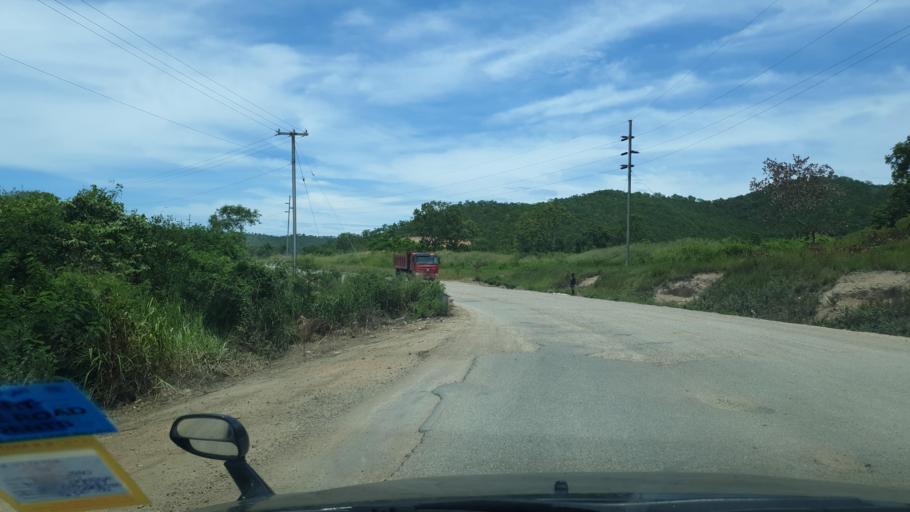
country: PG
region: National Capital
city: Port Moresby
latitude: -9.4192
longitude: 147.0957
